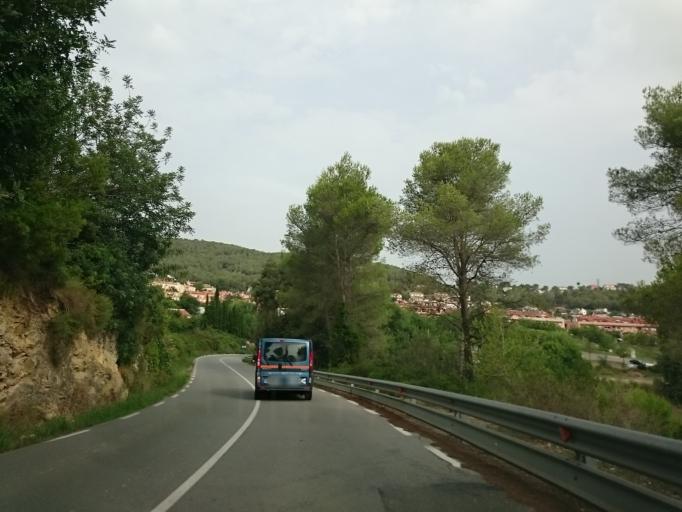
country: ES
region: Catalonia
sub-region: Provincia de Barcelona
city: Sant Pere de Ribes
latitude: 41.2969
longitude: 1.7802
